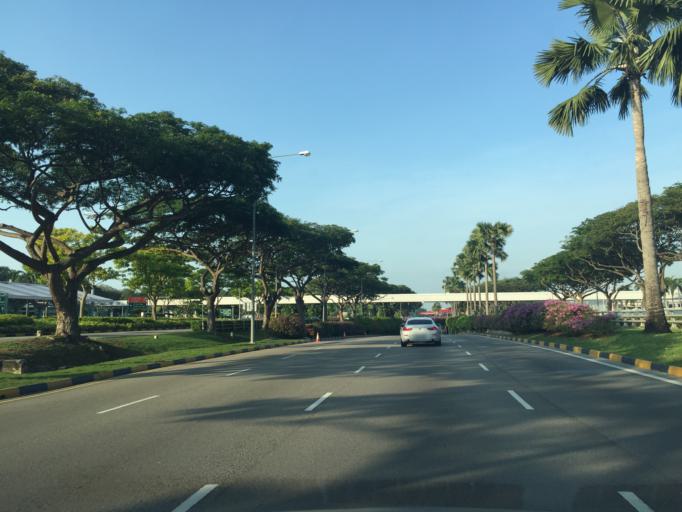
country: SG
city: Singapore
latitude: 1.3535
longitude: 103.9870
